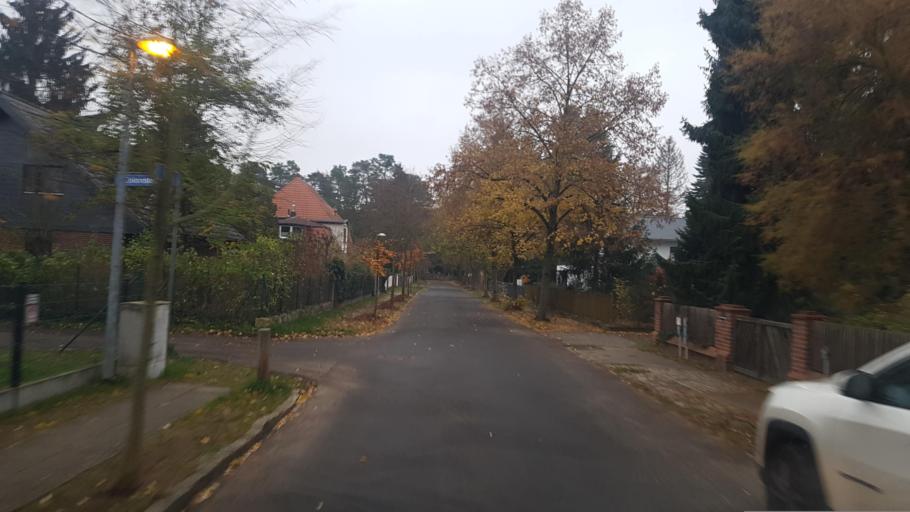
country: DE
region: Brandenburg
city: Michendorf
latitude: 52.3222
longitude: 13.0280
